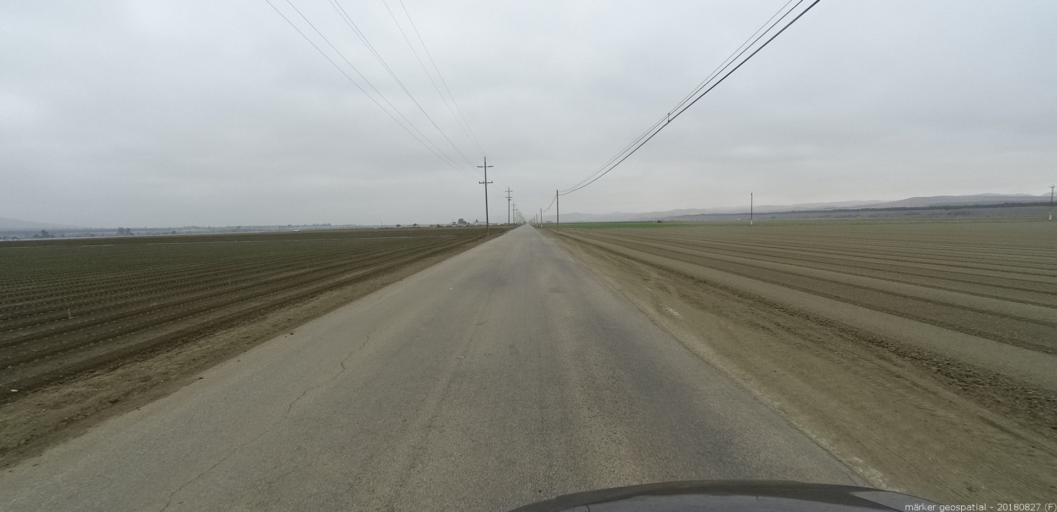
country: US
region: California
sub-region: Monterey County
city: King City
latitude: 36.2317
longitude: -121.1415
